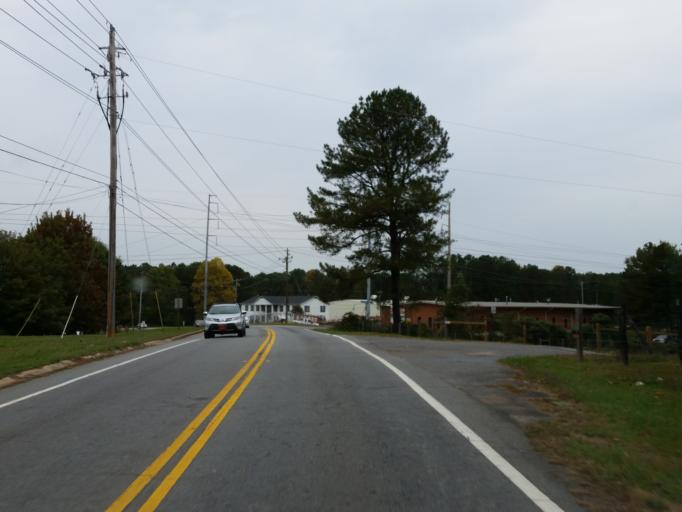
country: US
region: Georgia
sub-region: Cherokee County
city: Woodstock
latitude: 34.0560
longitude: -84.5150
